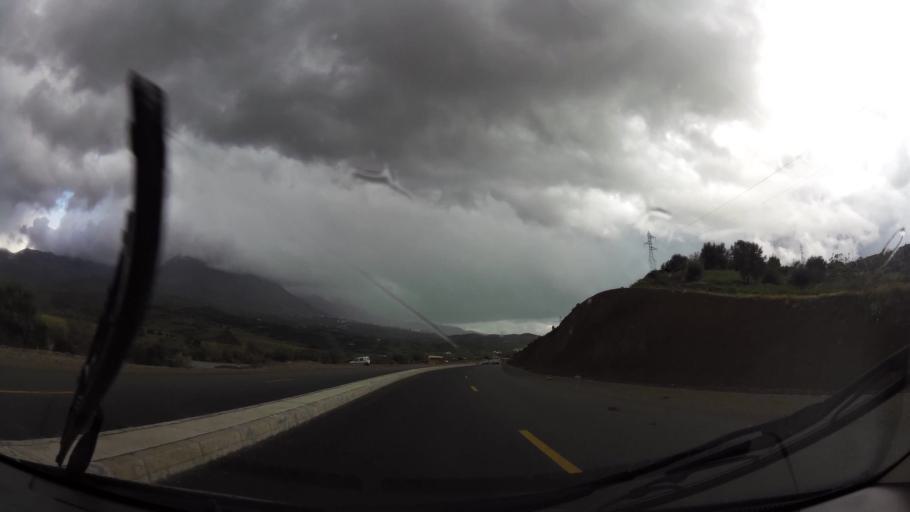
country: MA
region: Tanger-Tetouan
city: Chefchaouene
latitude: 35.2043
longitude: -5.3158
